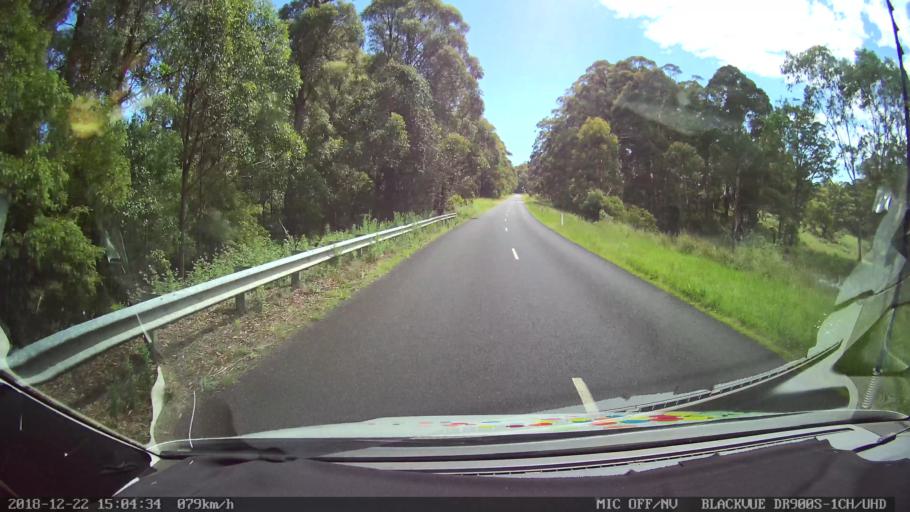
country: AU
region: New South Wales
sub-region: Bellingen
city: Dorrigo
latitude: -30.2761
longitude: 152.4374
